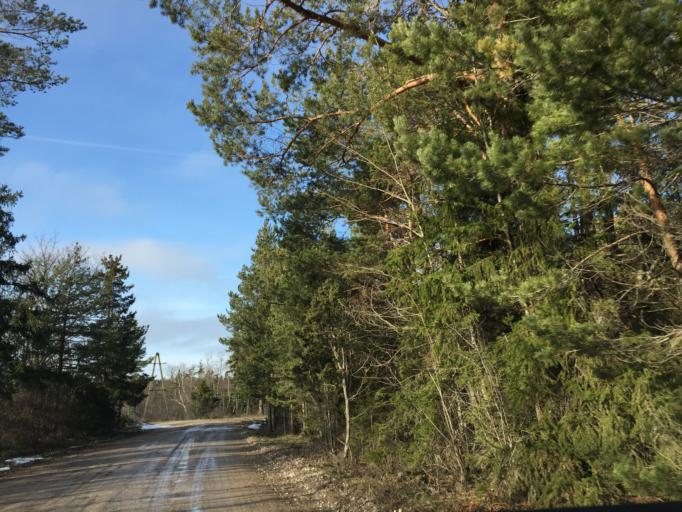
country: EE
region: Saare
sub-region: Kuressaare linn
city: Kuressaare
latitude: 58.4686
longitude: 21.9904
